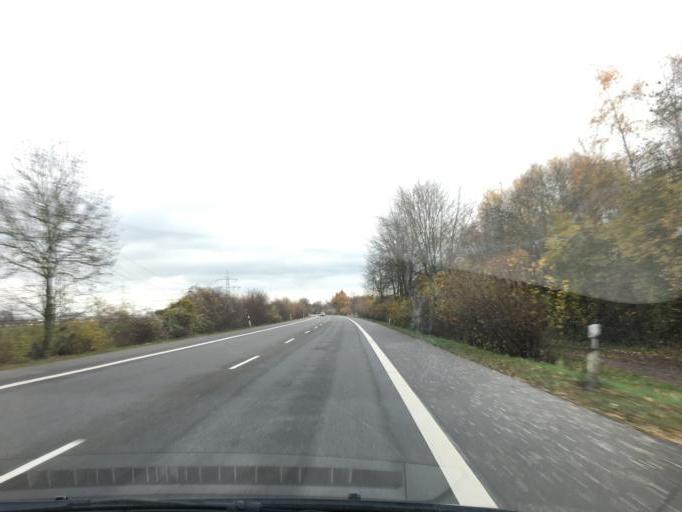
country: DE
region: North Rhine-Westphalia
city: Julich
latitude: 50.8973
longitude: 6.3779
